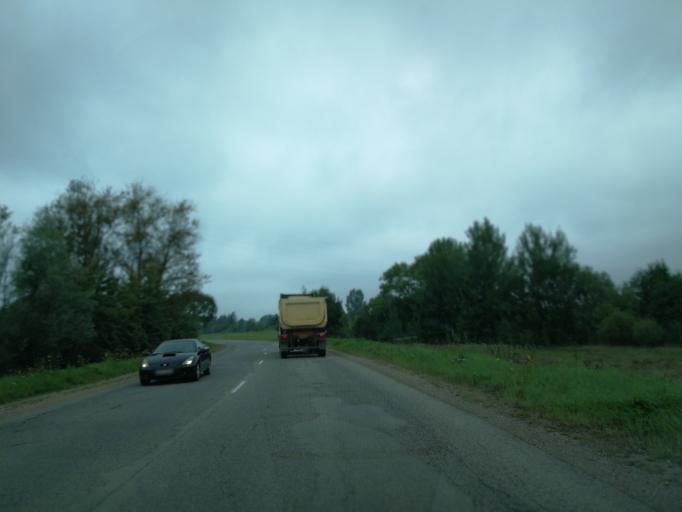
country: LV
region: Jekabpils Rajons
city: Jekabpils
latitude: 56.5012
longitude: 25.8991
